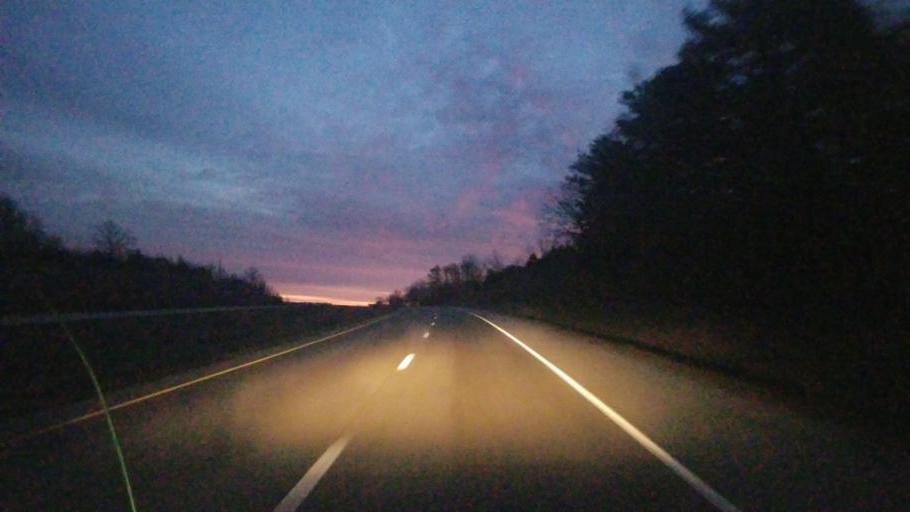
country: US
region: Missouri
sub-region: Howell County
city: Mountain View
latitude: 36.9911
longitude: -91.5228
